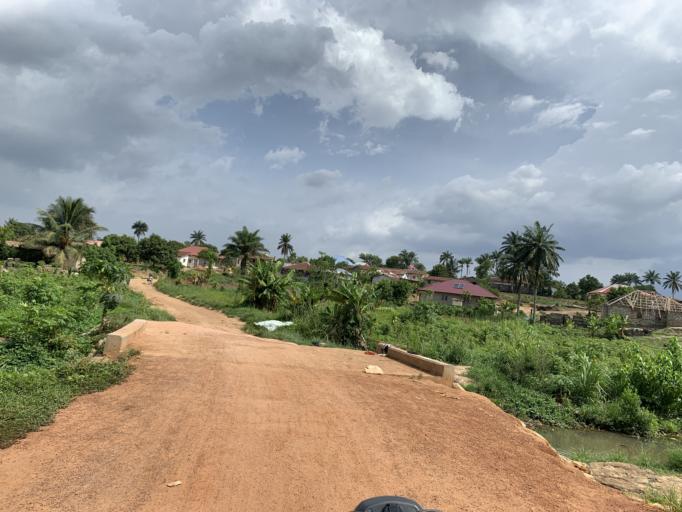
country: SL
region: Western Area
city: Waterloo
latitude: 8.3508
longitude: -13.0497
